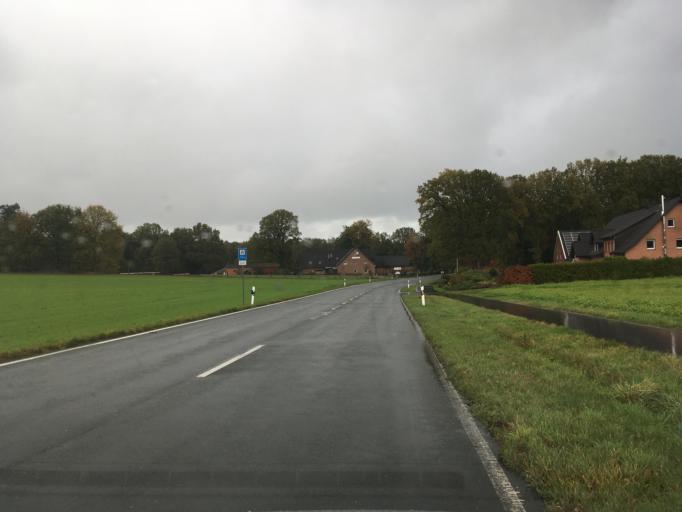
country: DE
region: North Rhine-Westphalia
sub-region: Regierungsbezirk Munster
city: Klein Reken
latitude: 51.8483
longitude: 7.0297
